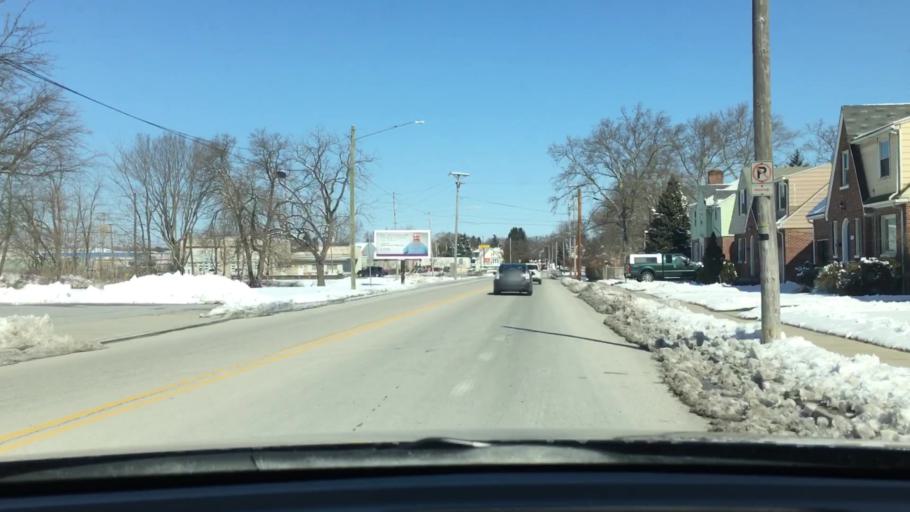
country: US
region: Pennsylvania
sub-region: York County
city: West York
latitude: 39.9684
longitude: -76.7514
